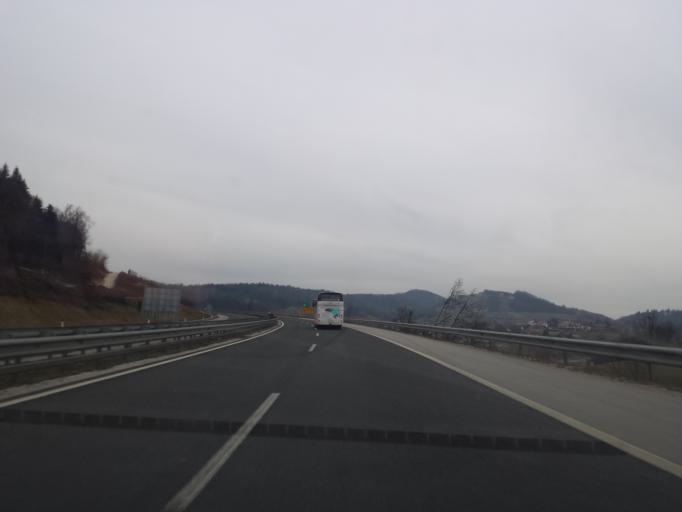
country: SI
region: Mirna Pec
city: Mirna Pec
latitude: 45.8727
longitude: 15.1086
